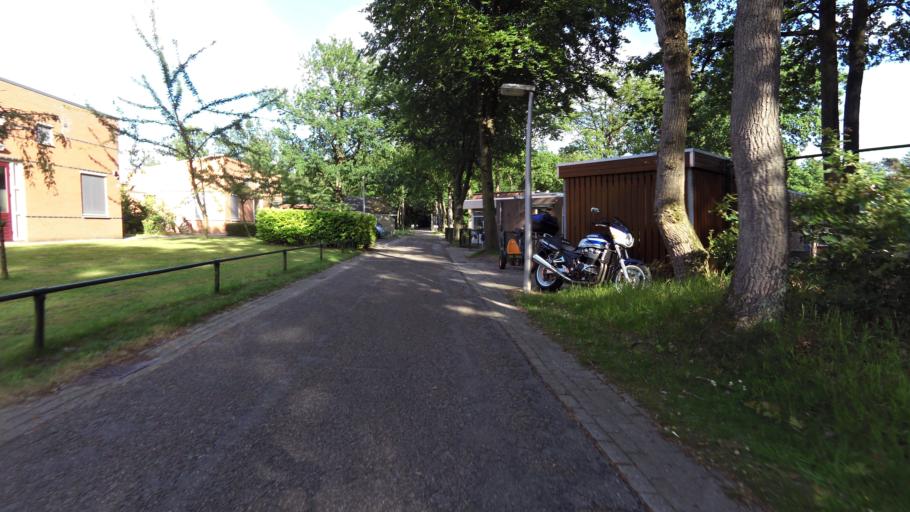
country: NL
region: North Holland
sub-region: Gemeente Laren
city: Laren
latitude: 52.2191
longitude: 5.2258
